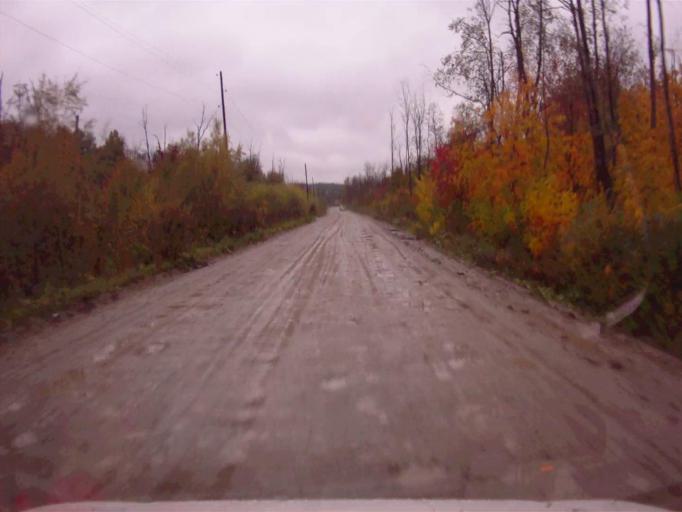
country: RU
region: Chelyabinsk
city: Kyshtym
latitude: 55.7349
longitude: 60.5158
